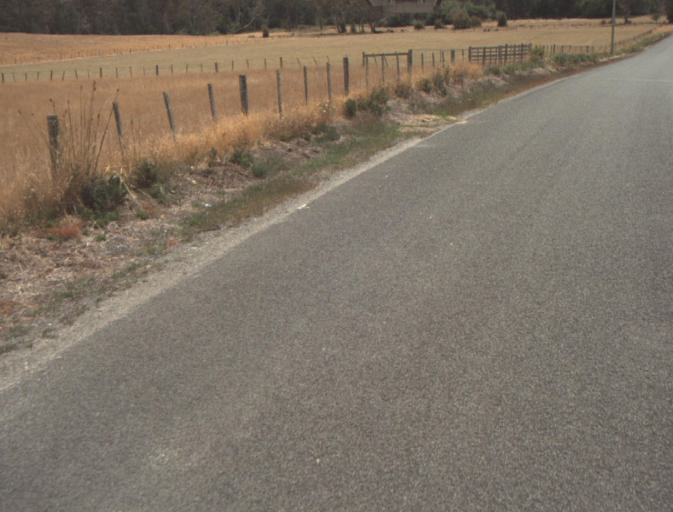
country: AU
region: Tasmania
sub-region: Launceston
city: Mayfield
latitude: -41.2233
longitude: 147.1372
